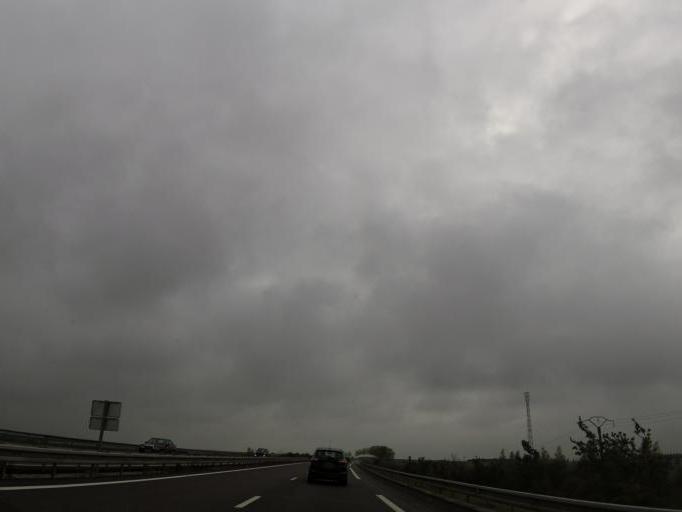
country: FR
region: Champagne-Ardenne
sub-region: Departement de la Marne
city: Fagnieres
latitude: 49.0385
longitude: 4.3476
